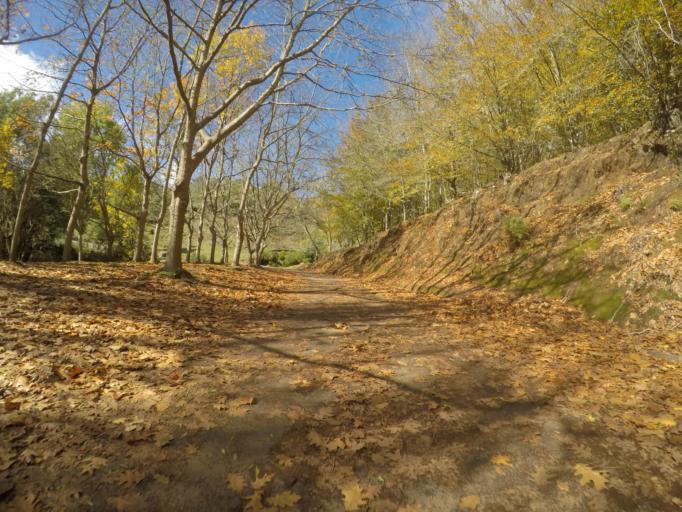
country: PT
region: Madeira
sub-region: Funchal
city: Nossa Senhora do Monte
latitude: 32.6988
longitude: -16.8821
